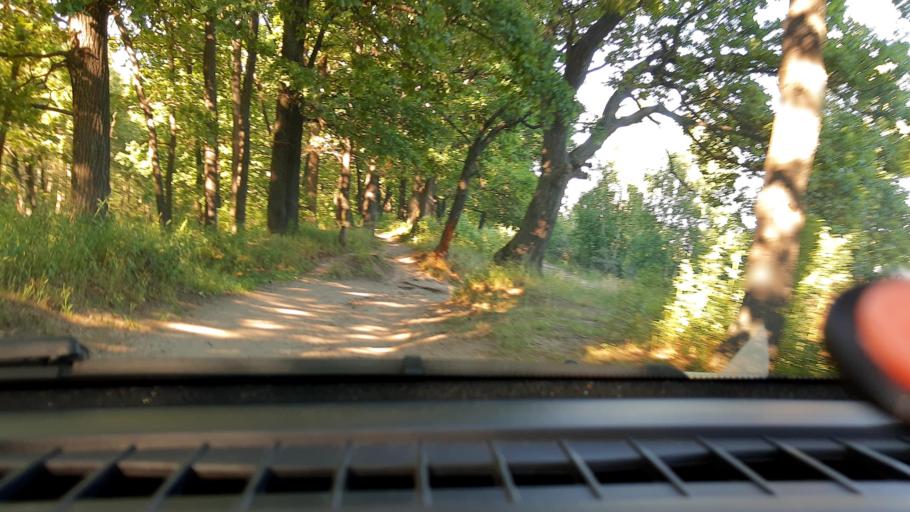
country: RU
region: Nizjnij Novgorod
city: Burevestnik
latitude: 56.2004
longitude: 43.8266
